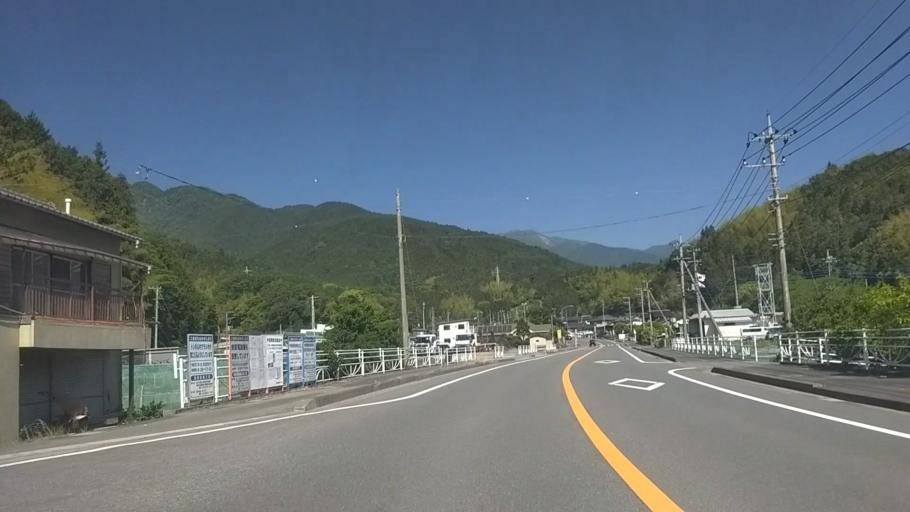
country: JP
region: Shizuoka
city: Fujinomiya
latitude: 35.2625
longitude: 138.4672
